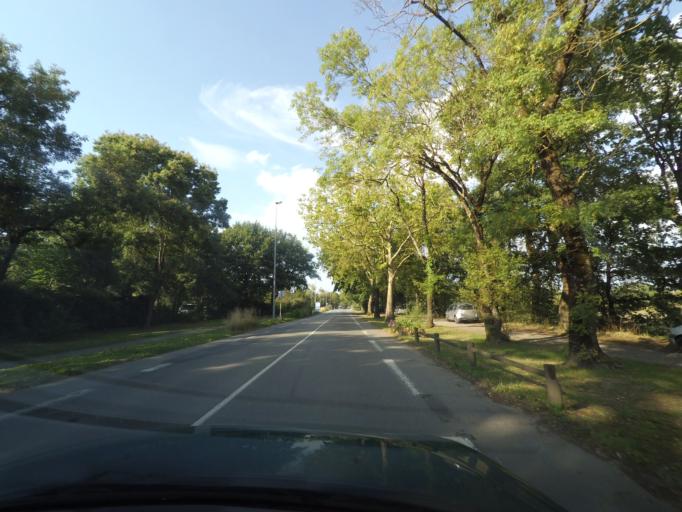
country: FR
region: Pays de la Loire
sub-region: Departement de la Loire-Atlantique
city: Saint-Philbert-de-Grand-Lieu
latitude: 47.0421
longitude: -1.6404
